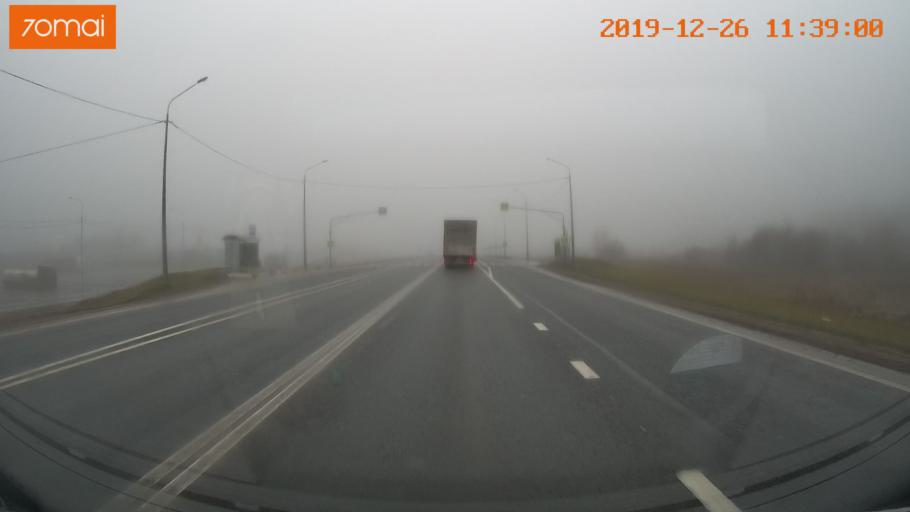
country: RU
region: Vologda
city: Sheksna
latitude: 59.2110
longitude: 38.6087
